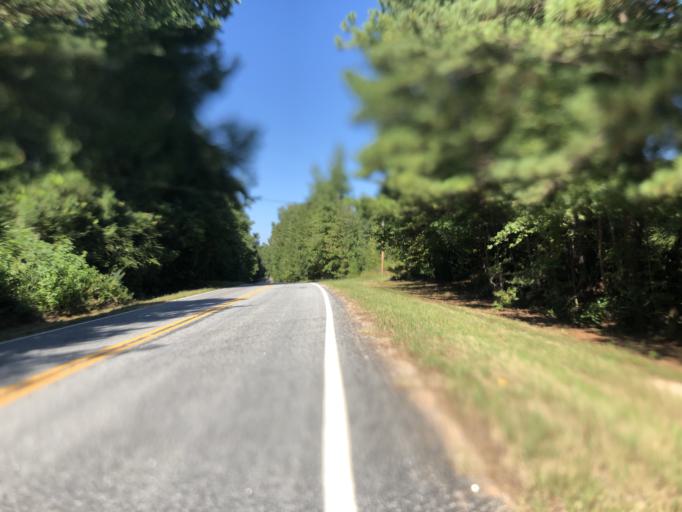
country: US
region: Georgia
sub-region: Heard County
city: Franklin
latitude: 33.3781
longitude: -84.9741
